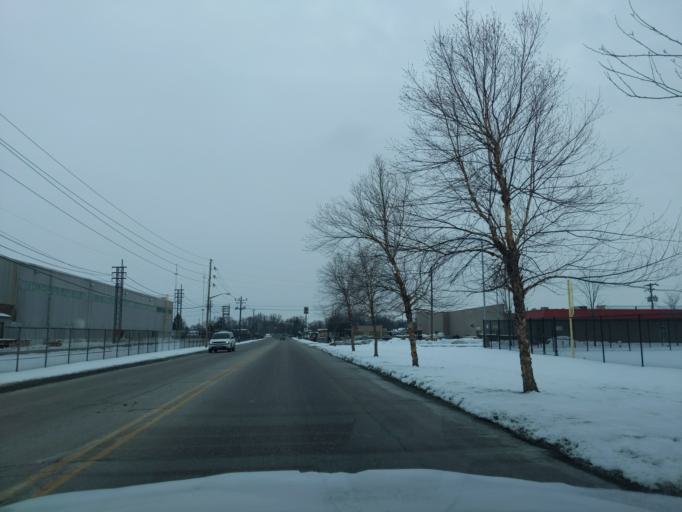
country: US
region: Indiana
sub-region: Tippecanoe County
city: Lafayette
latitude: 40.3989
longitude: -86.8671
